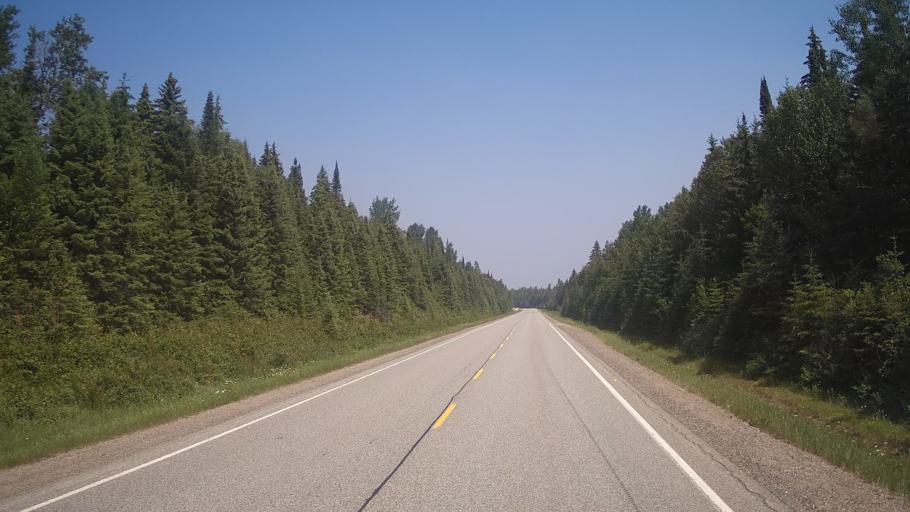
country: CA
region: Ontario
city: Timmins
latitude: 48.2112
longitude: -81.5742
